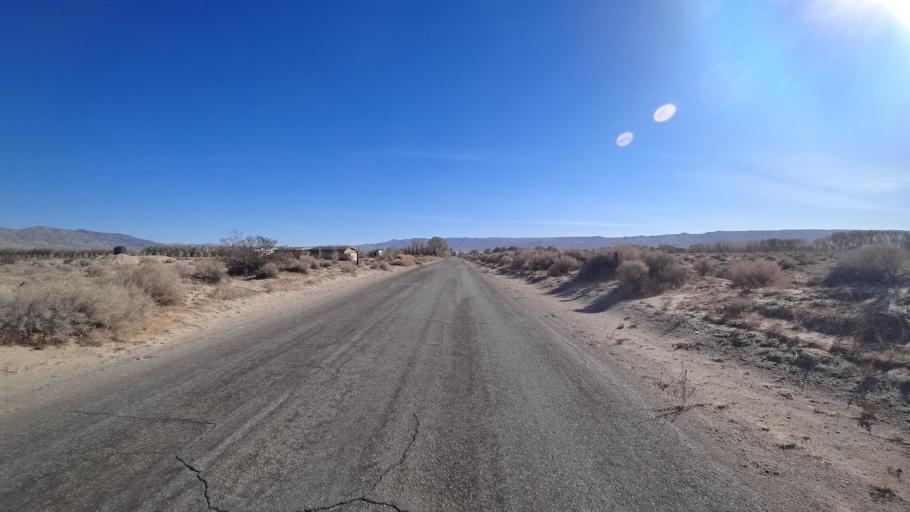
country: US
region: California
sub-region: Kern County
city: California City
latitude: 35.3158
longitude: -117.9350
